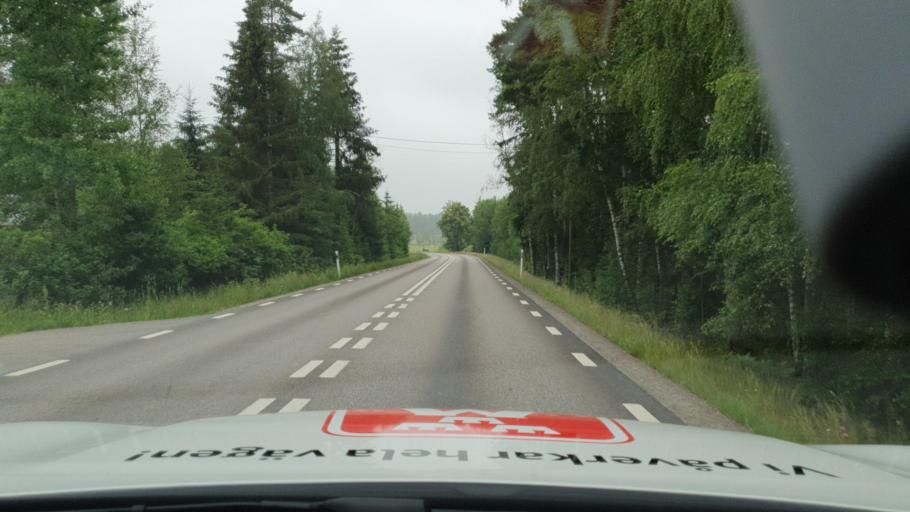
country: SE
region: Vaermland
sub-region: Karlstads Kommun
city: Edsvalla
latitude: 59.5935
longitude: 13.1660
